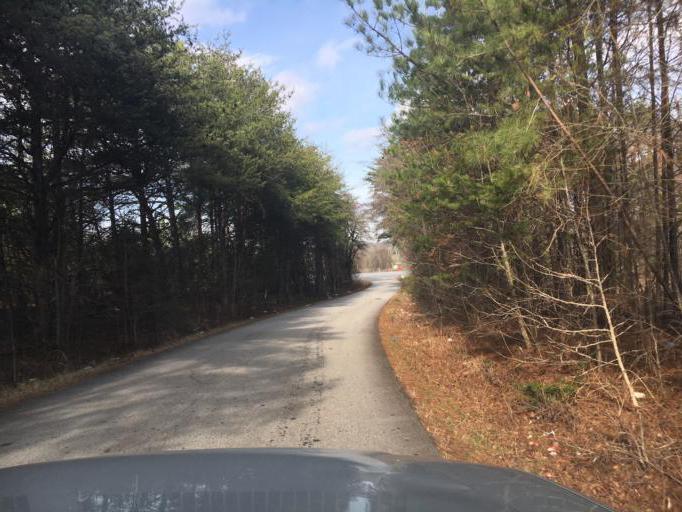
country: US
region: South Carolina
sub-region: Spartanburg County
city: Duncan
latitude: 34.9544
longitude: -82.1639
